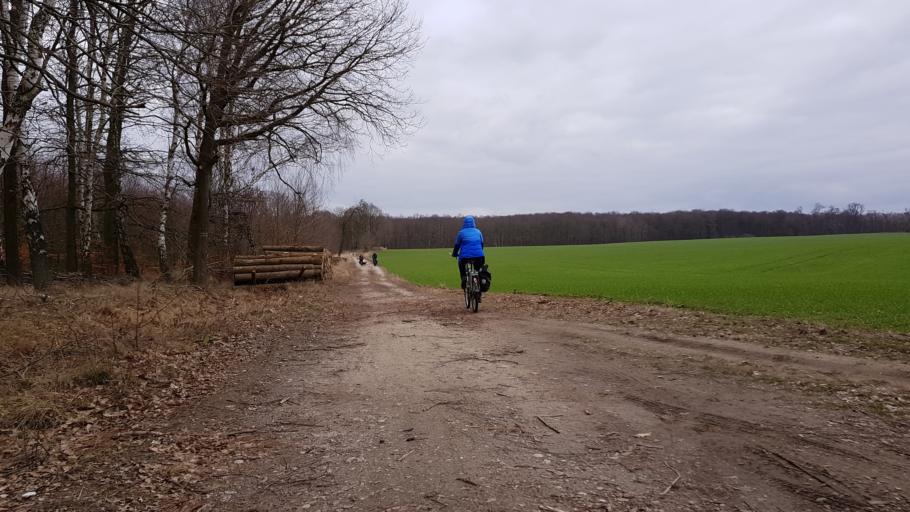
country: PL
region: West Pomeranian Voivodeship
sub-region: Powiat gryfinski
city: Banie
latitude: 53.0755
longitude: 14.7282
